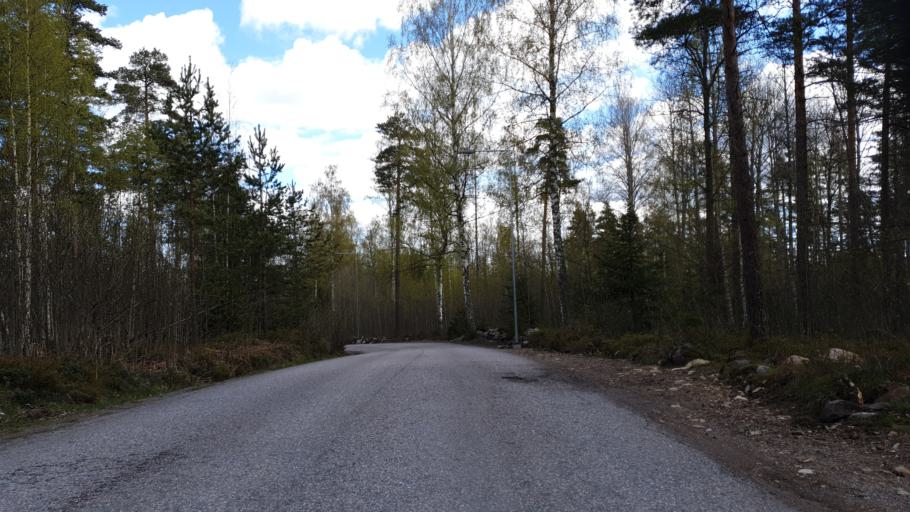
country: FI
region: Uusimaa
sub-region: Helsinki
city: Nurmijaervi
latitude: 60.3480
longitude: 24.8432
